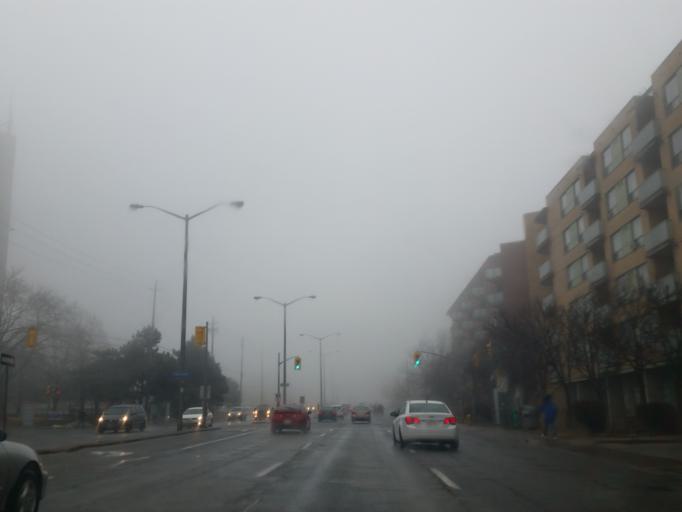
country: CA
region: Ontario
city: Scarborough
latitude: 43.7364
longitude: -79.2199
